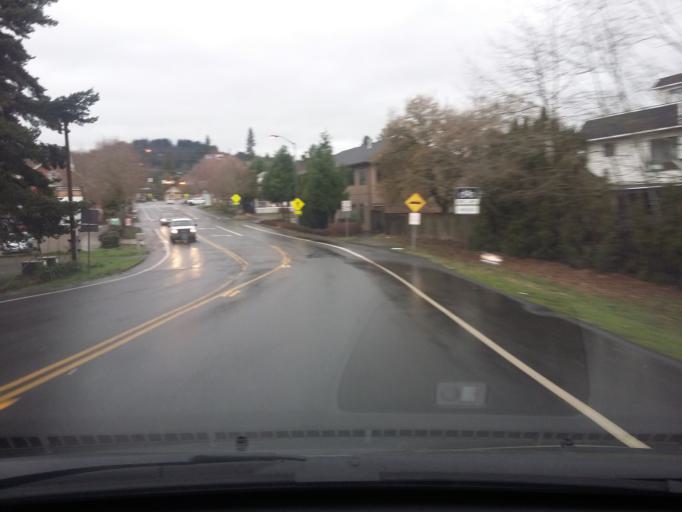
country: US
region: Washington
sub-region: Clark County
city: Washougal
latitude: 45.5771
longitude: -122.3559
